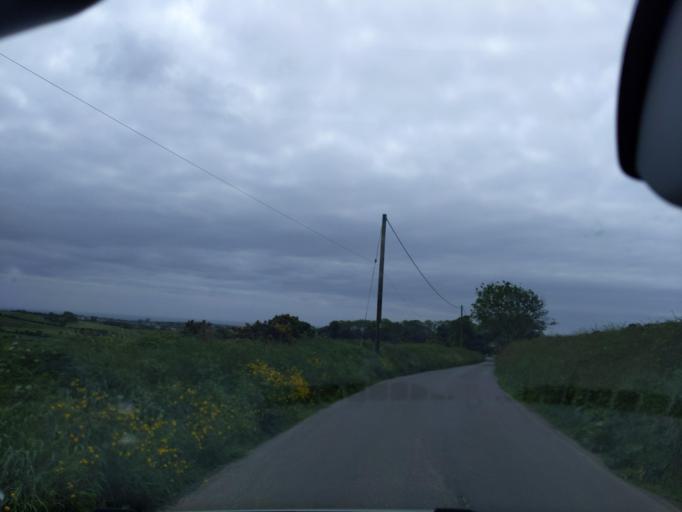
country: IM
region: Douglas
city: Douglas
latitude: 54.1484
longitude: -4.5617
